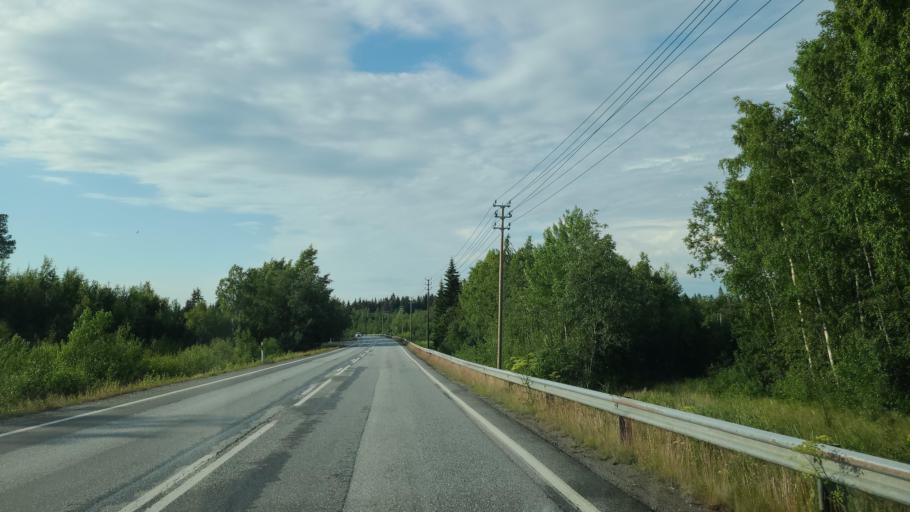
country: FI
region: Ostrobothnia
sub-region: Vaasa
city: Vaasa
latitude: 63.1871
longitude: 21.5660
